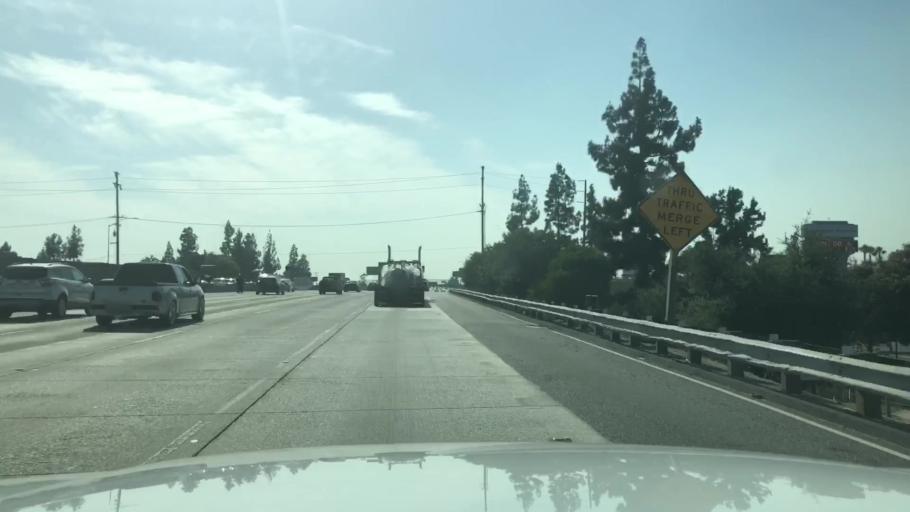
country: US
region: California
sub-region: Los Angeles County
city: Duarte
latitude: 34.1351
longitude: -117.9753
